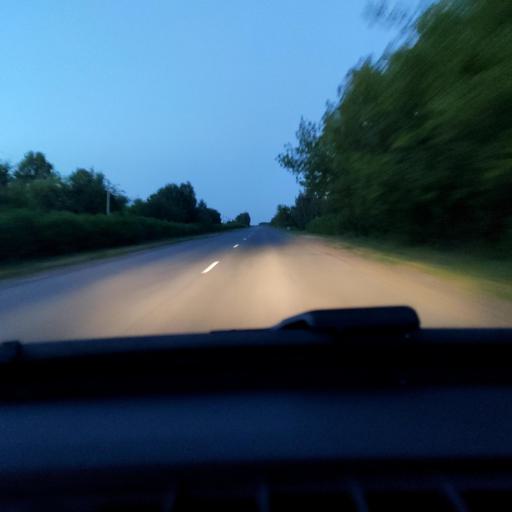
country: RU
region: Lipetsk
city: Zadonsk
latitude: 52.2944
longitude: 38.7777
